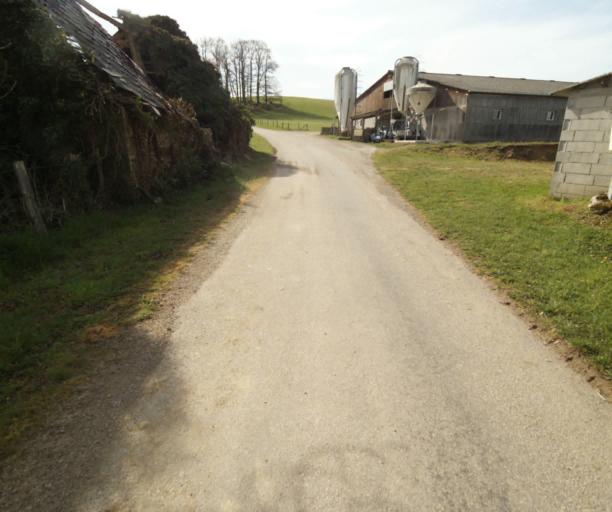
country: FR
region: Limousin
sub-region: Departement de la Correze
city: Correze
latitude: 45.3541
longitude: 1.8655
